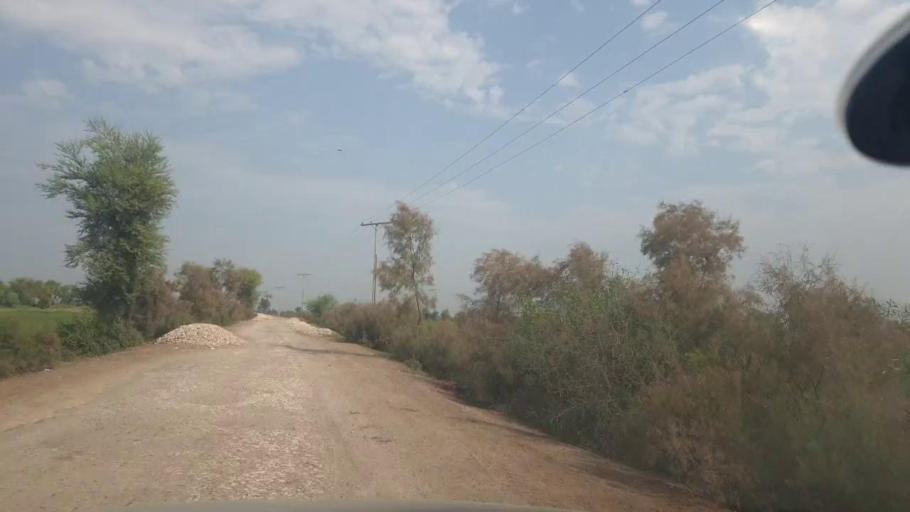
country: PK
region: Balochistan
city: Mehrabpur
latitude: 28.0659
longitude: 68.1035
